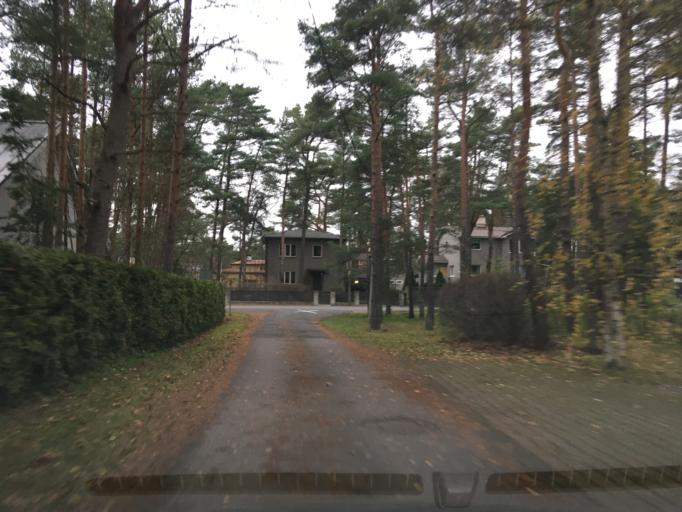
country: EE
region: Harju
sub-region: Tallinna linn
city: Tallinn
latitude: 59.3767
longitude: 24.7008
